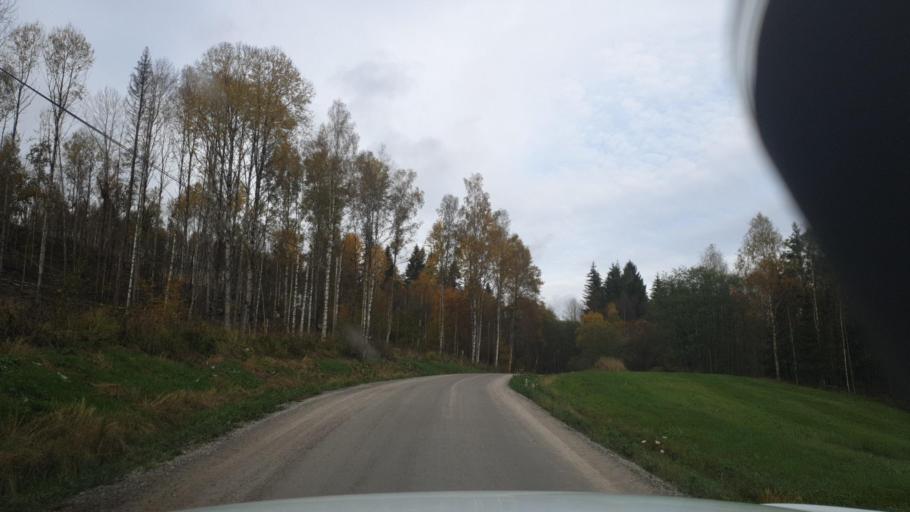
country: SE
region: Vaermland
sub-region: Sunne Kommun
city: Sunne
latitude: 59.6958
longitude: 12.8852
